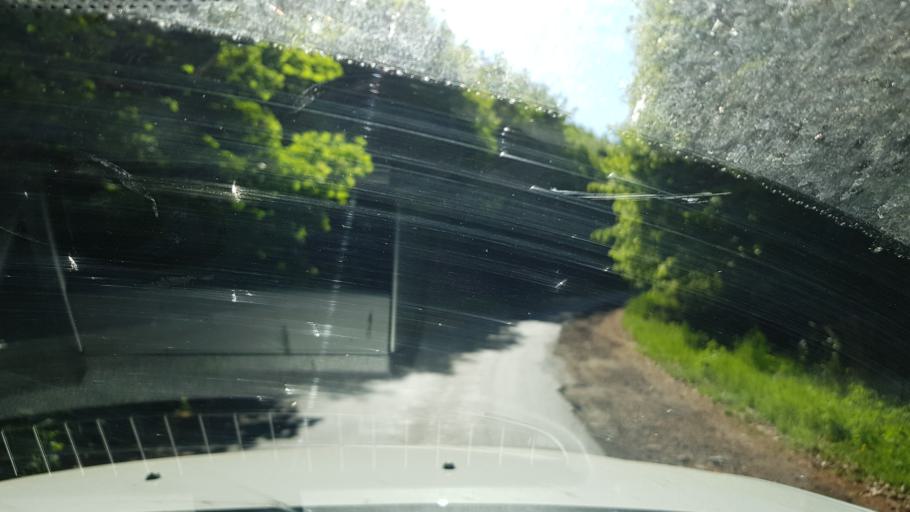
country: PL
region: West Pomeranian Voivodeship
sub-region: Powiat kolobrzeski
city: Goscino
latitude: 54.0111
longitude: 15.6192
